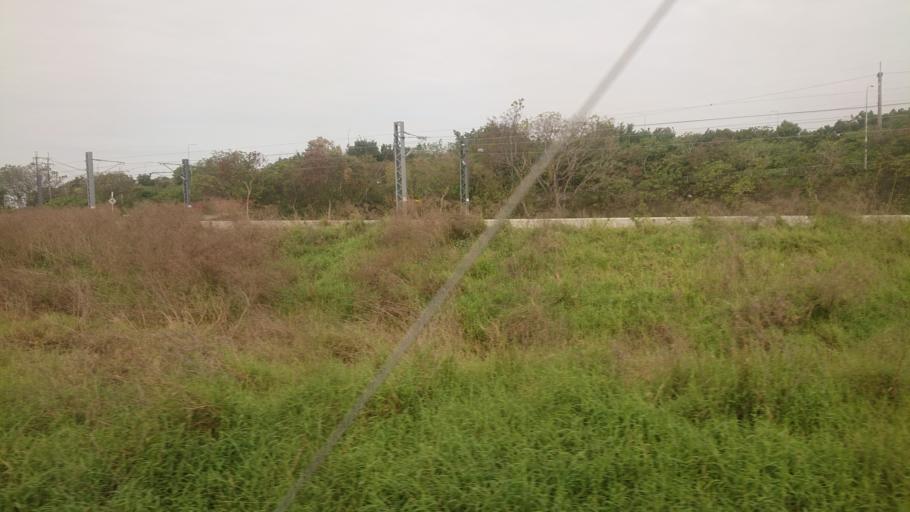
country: TW
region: Taiwan
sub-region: Changhua
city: Chang-hua
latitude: 24.1154
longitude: 120.5821
